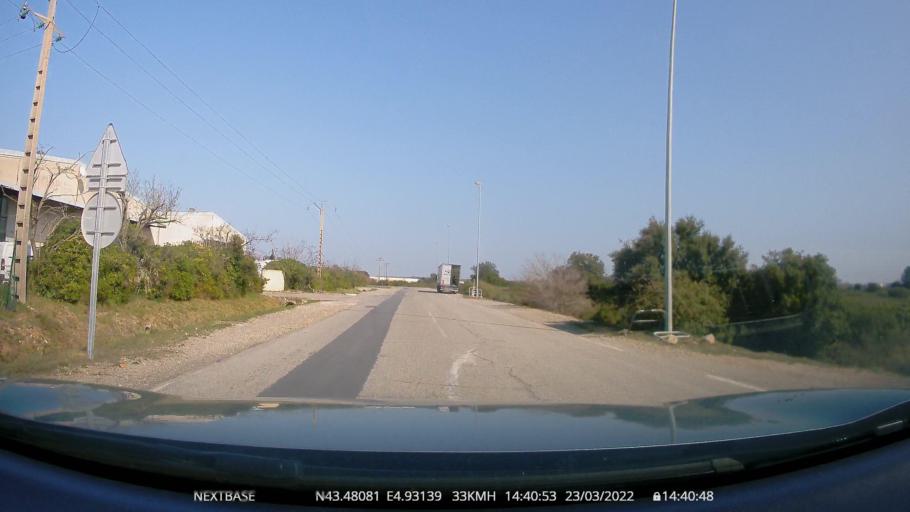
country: FR
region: Provence-Alpes-Cote d'Azur
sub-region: Departement des Bouches-du-Rhone
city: Fos-sur-Mer
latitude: 43.4808
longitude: 4.9310
